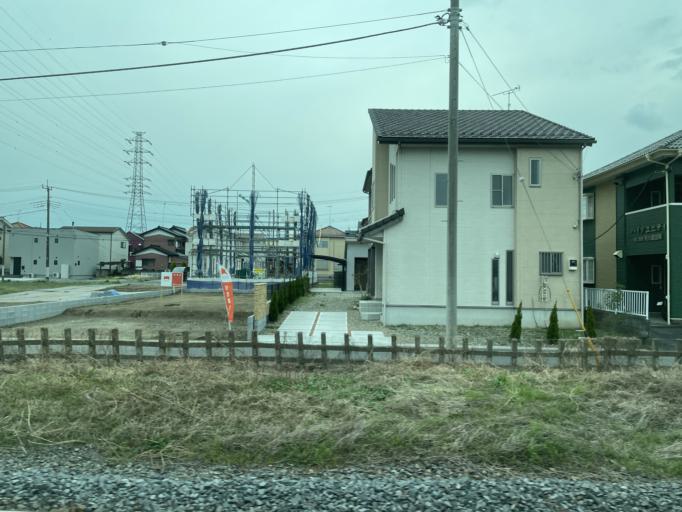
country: JP
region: Saitama
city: Sugito
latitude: 36.0285
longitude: 139.7200
